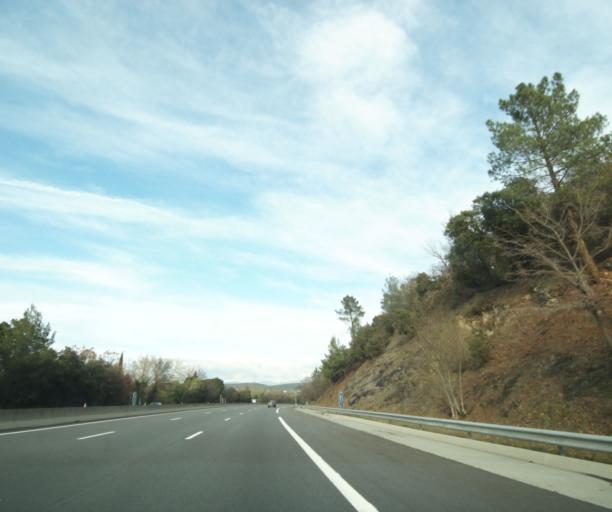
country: FR
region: Provence-Alpes-Cote d'Azur
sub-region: Departement du Var
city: Les Arcs
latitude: 43.4350
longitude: 6.4674
